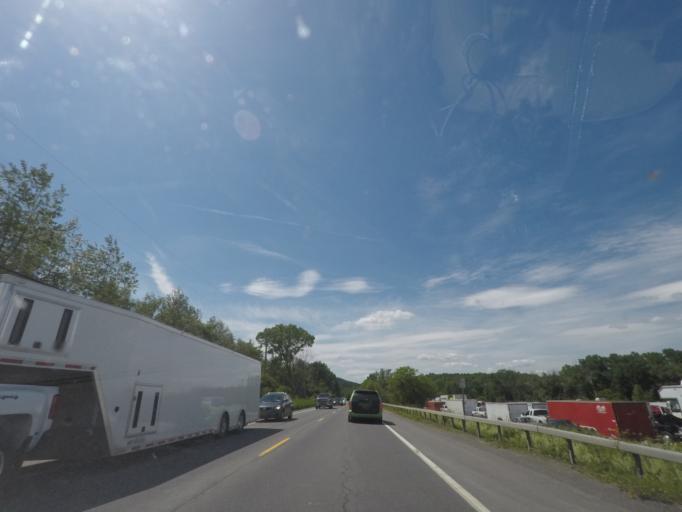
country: US
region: New York
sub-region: Rensselaer County
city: Nassau
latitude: 42.4920
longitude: -73.4914
